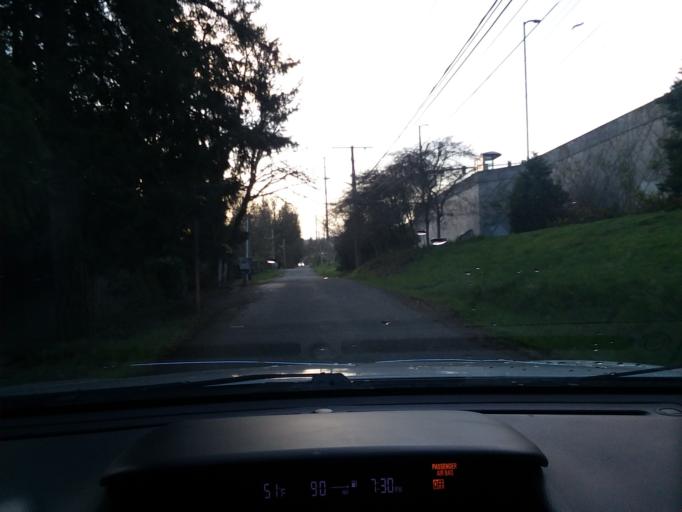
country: US
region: Washington
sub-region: King County
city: Kenmore
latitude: 47.7539
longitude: -122.2294
